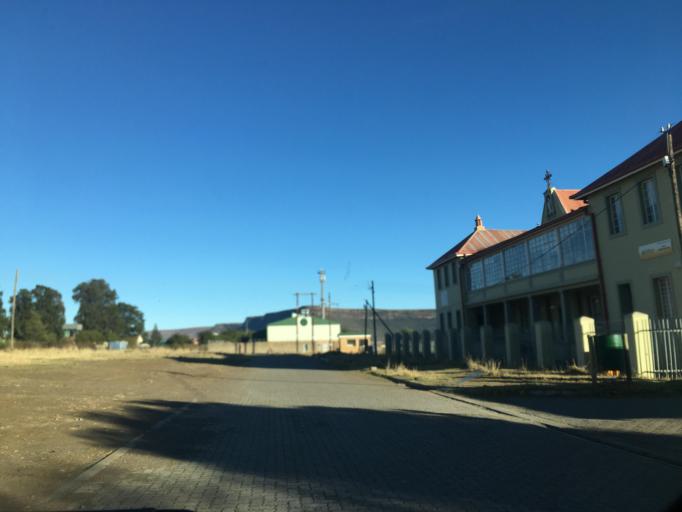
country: ZA
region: Eastern Cape
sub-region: Chris Hani District Municipality
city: Cala
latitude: -31.5246
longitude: 27.6992
